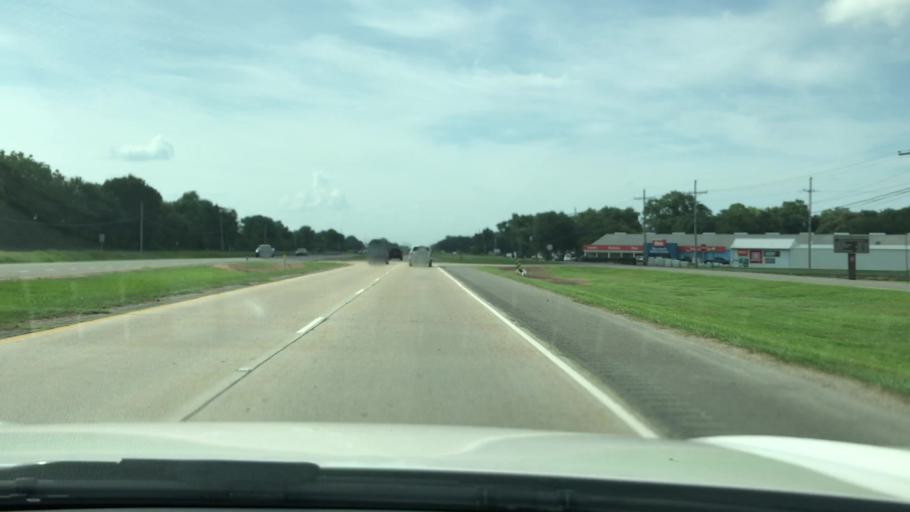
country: US
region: Louisiana
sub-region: Iberville Parish
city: Plaquemine
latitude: 30.3066
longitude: -91.2454
